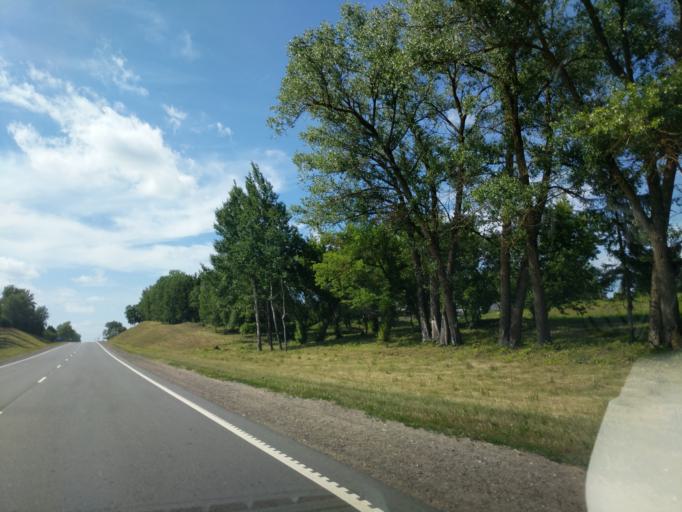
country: BY
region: Minsk
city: Syomkava
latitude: 54.1059
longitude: 27.4677
